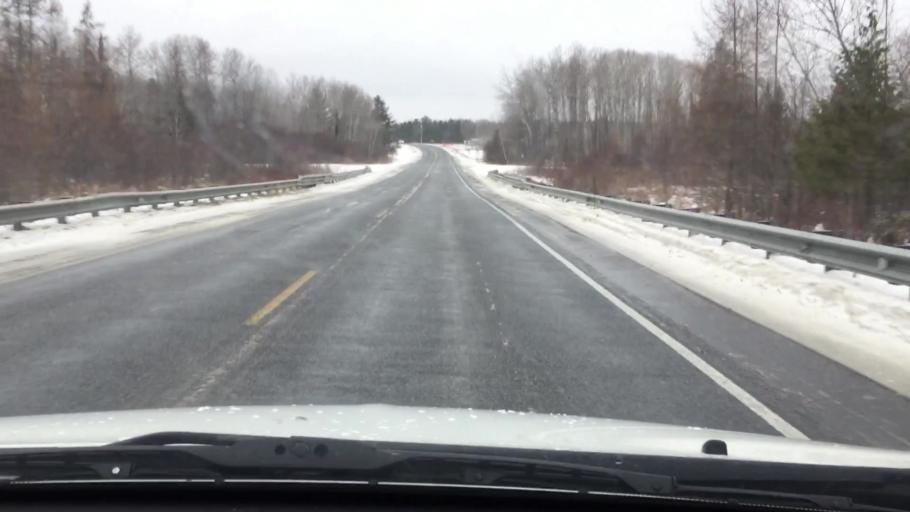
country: US
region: Michigan
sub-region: Wexford County
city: Cadillac
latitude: 44.1179
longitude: -85.4421
